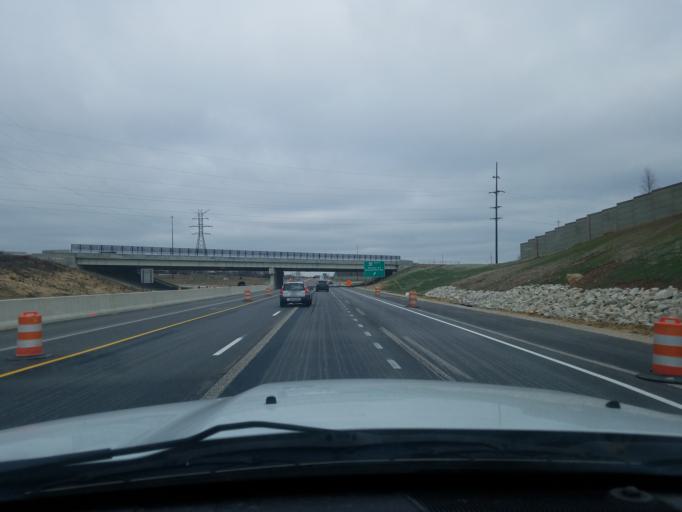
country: US
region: Indiana
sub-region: Monroe County
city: Bloomington
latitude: 39.1461
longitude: -86.5729
